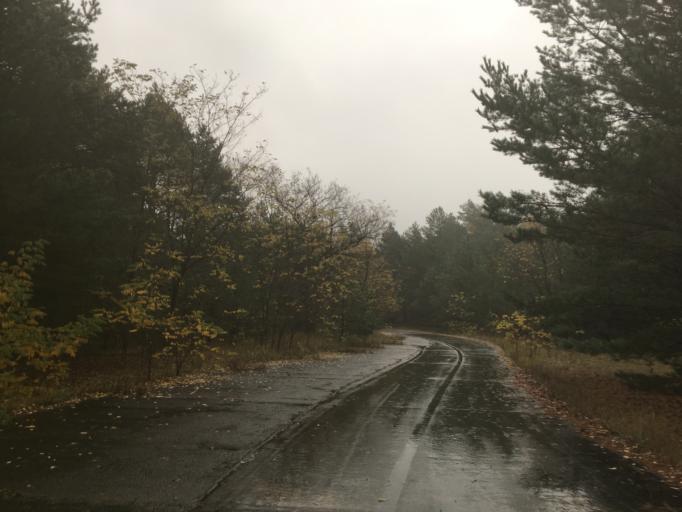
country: DE
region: Brandenburg
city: Halbe
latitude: 52.0309
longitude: 13.7634
